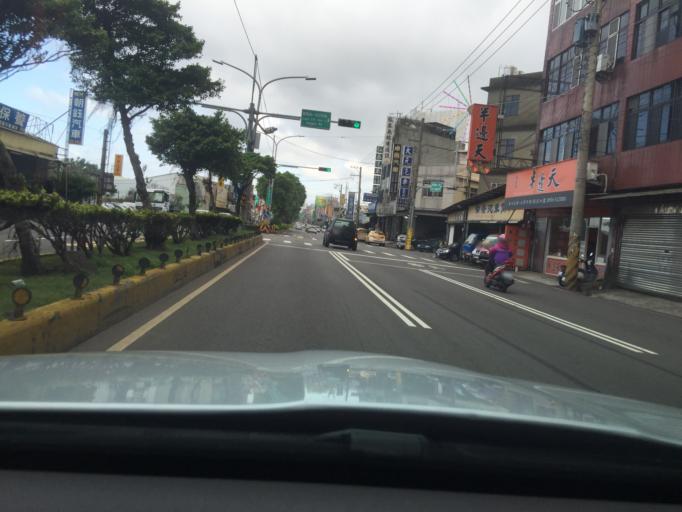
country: TW
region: Taiwan
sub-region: Hsinchu
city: Hsinchu
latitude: 24.8148
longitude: 120.9819
